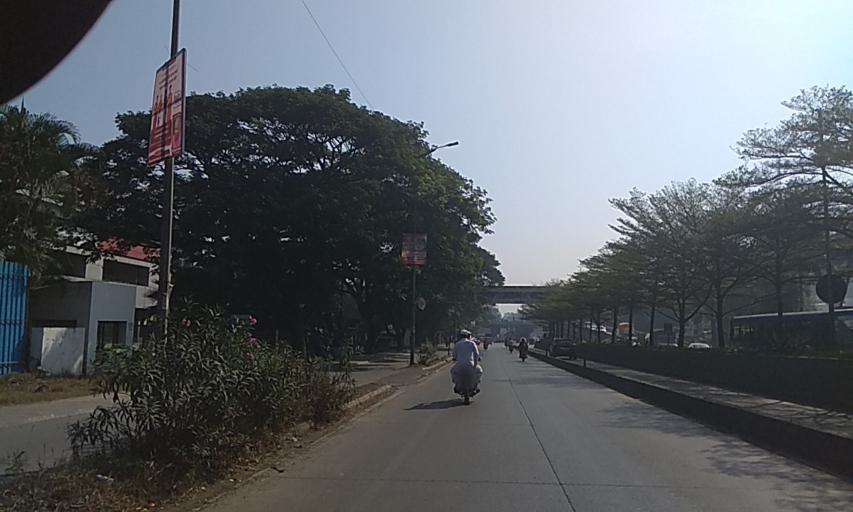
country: IN
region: Maharashtra
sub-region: Pune Division
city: Pune
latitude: 18.5032
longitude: 73.9250
